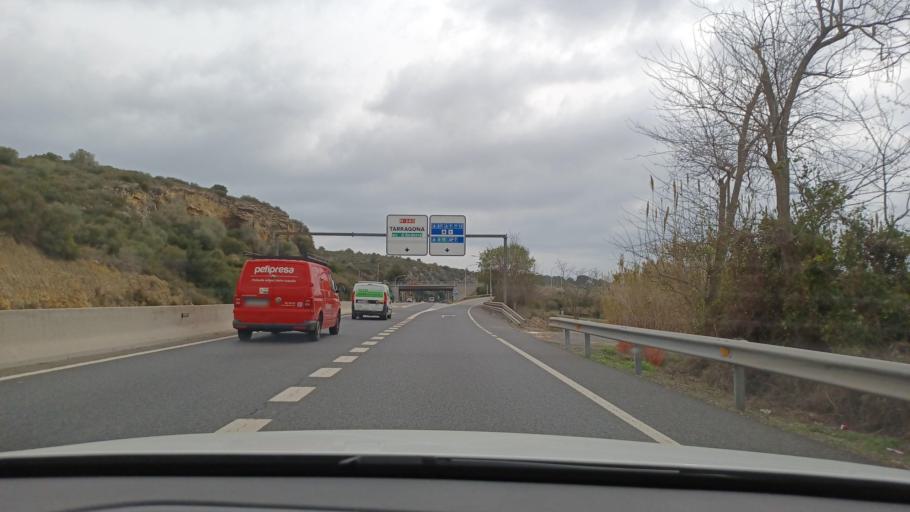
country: ES
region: Catalonia
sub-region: Provincia de Tarragona
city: Constanti
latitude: 41.1435
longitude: 1.2393
